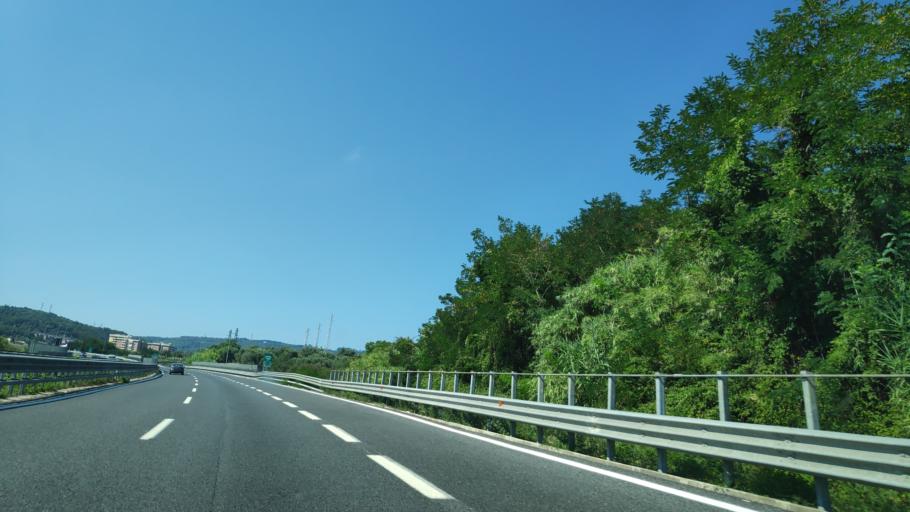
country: IT
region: Calabria
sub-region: Provincia di Reggio Calabria
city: Seminara
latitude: 38.3715
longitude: 15.8667
